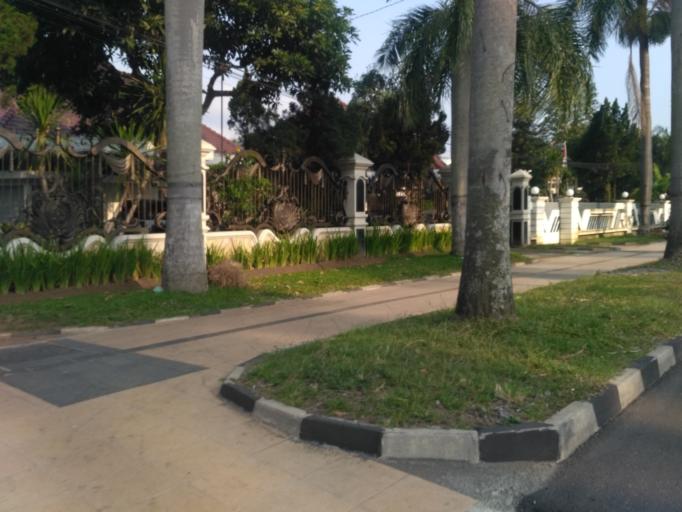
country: ID
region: East Java
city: Malang
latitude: -7.9705
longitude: 112.6227
